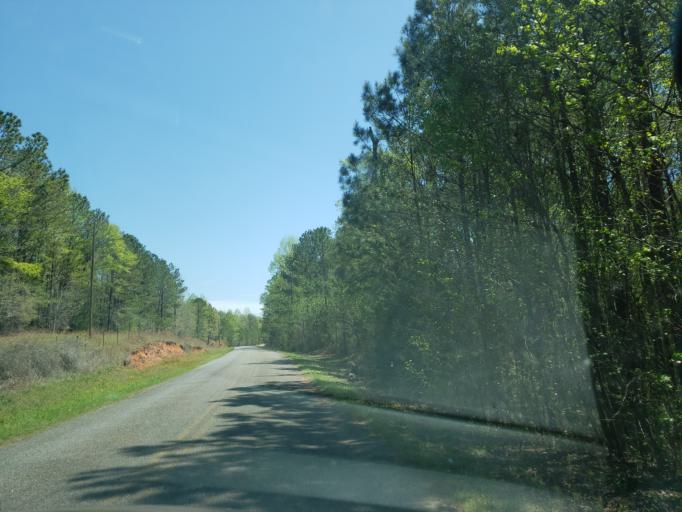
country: US
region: Alabama
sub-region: Tallapoosa County
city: Camp Hill
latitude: 32.6716
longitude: -85.7435
